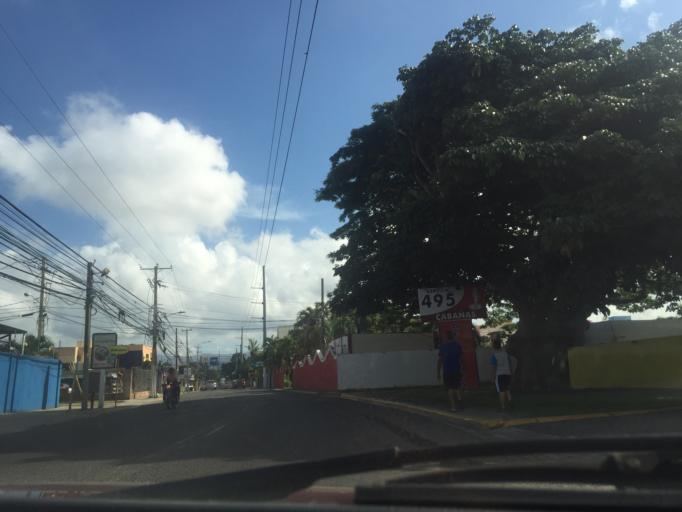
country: DO
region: Santiago
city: Santiago de los Caballeros
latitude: 19.4496
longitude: -70.6657
